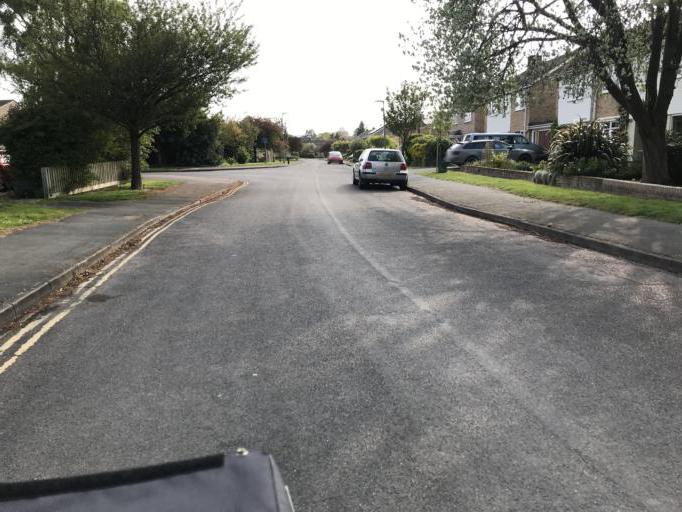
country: GB
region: England
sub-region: Cambridgeshire
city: Cambridge
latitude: 52.1773
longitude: 0.1553
